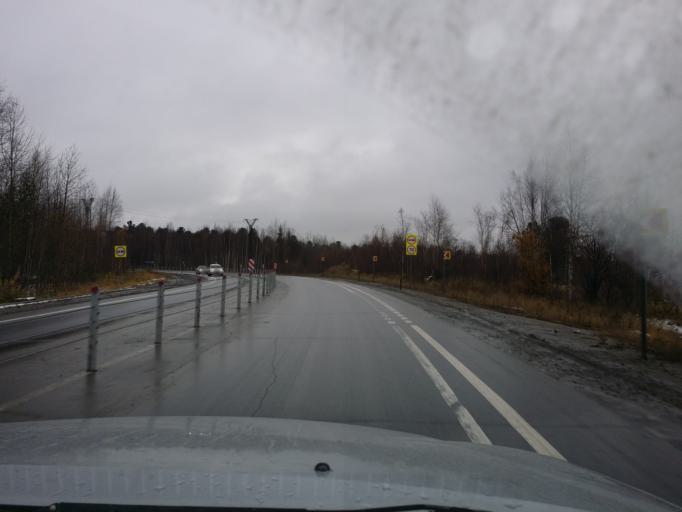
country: RU
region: Khanty-Mansiyskiy Avtonomnyy Okrug
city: Megion
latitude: 61.1101
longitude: 76.0352
